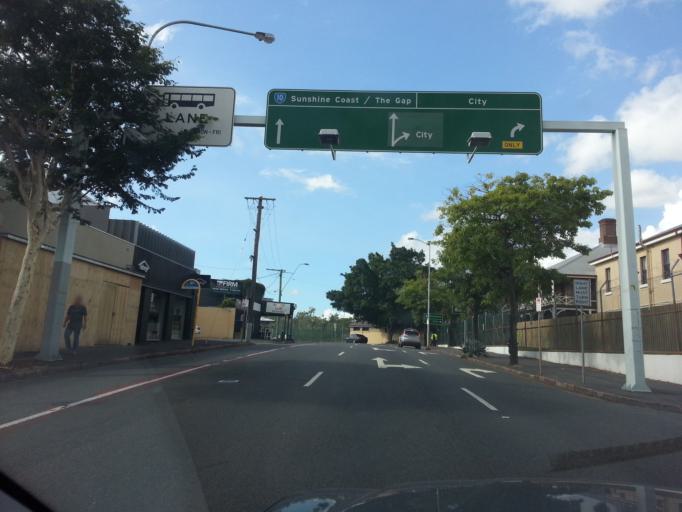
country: AU
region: Queensland
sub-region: Brisbane
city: Spring Hill
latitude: -27.4645
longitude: 153.0139
